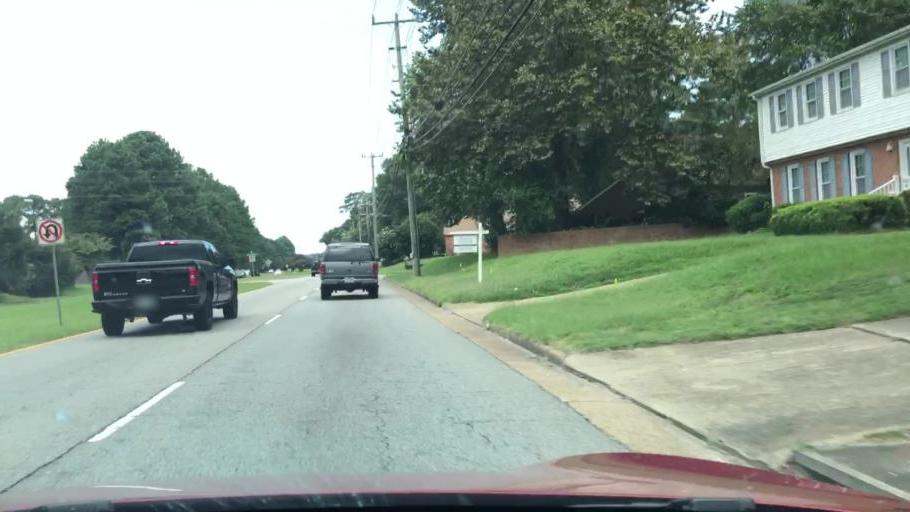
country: US
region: Virginia
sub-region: City of Chesapeake
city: Chesapeake
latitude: 36.8854
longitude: -76.1352
